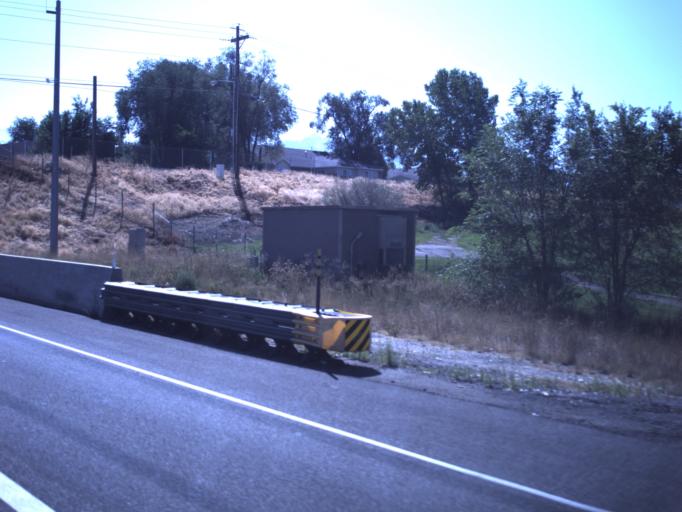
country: US
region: Utah
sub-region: Salt Lake County
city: Midvale
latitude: 40.6360
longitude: -111.9110
